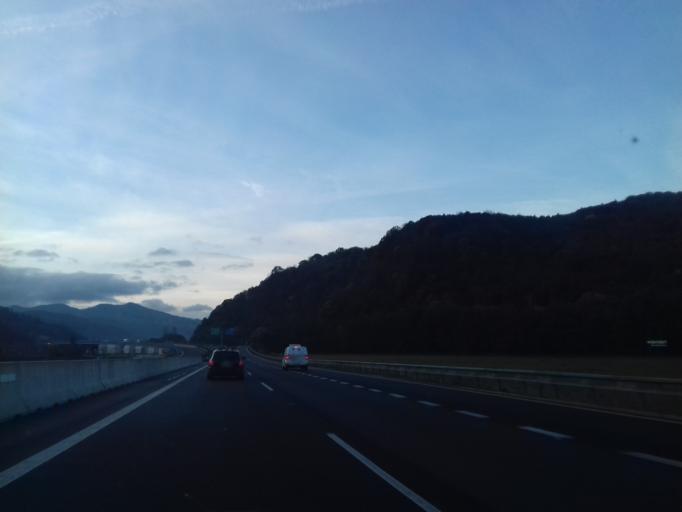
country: SK
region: Banskobystricky
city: Zarnovica
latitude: 48.5069
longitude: 18.7320
